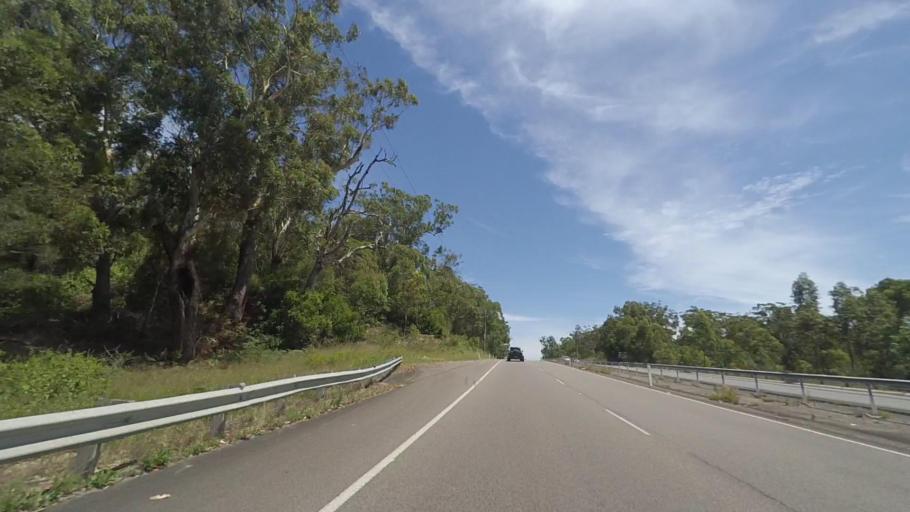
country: AU
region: New South Wales
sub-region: Port Stephens Shire
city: Anna Bay
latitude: -32.7682
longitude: 152.0123
